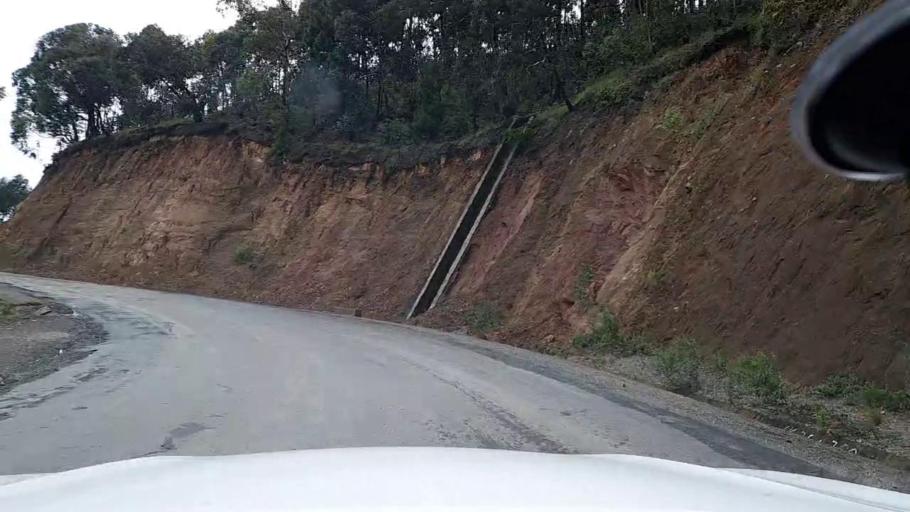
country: RW
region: Western Province
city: Kibuye
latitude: -2.0686
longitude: 29.5428
